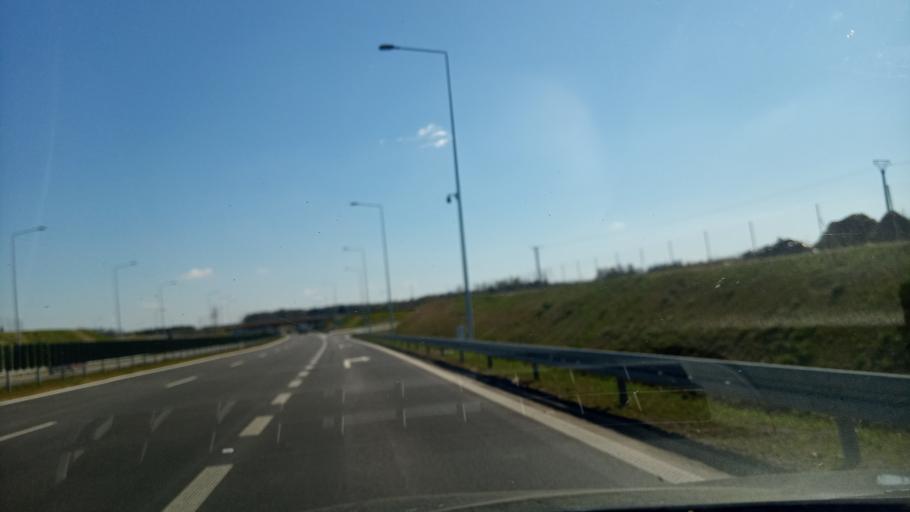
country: PL
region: West Pomeranian Voivodeship
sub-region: Powiat szczecinecki
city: Szczecinek
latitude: 53.6928
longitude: 16.7305
